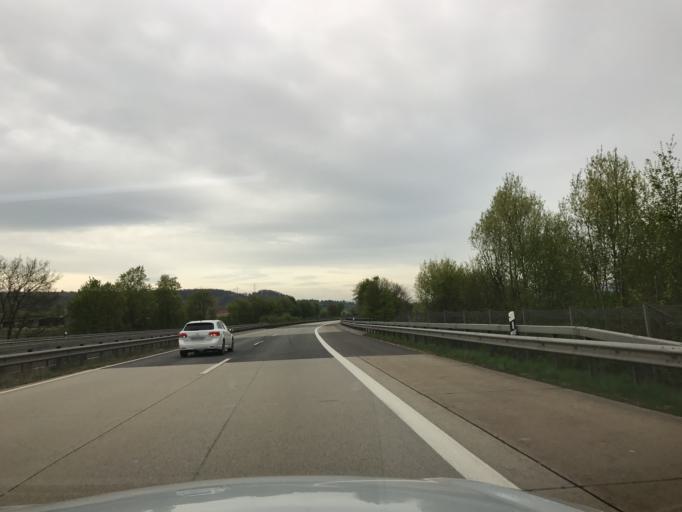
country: DE
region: Rheinland-Pfalz
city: Salmtal
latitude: 49.9329
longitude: 6.8735
